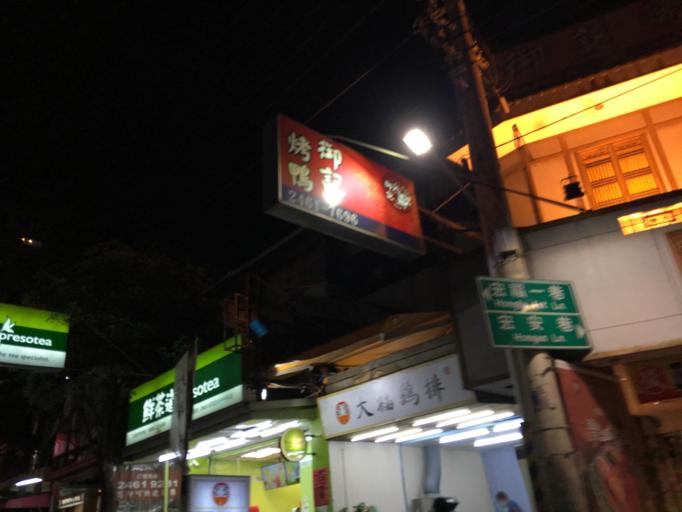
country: TW
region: Taiwan
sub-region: Taichung City
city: Taichung
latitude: 24.1881
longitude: 120.6181
